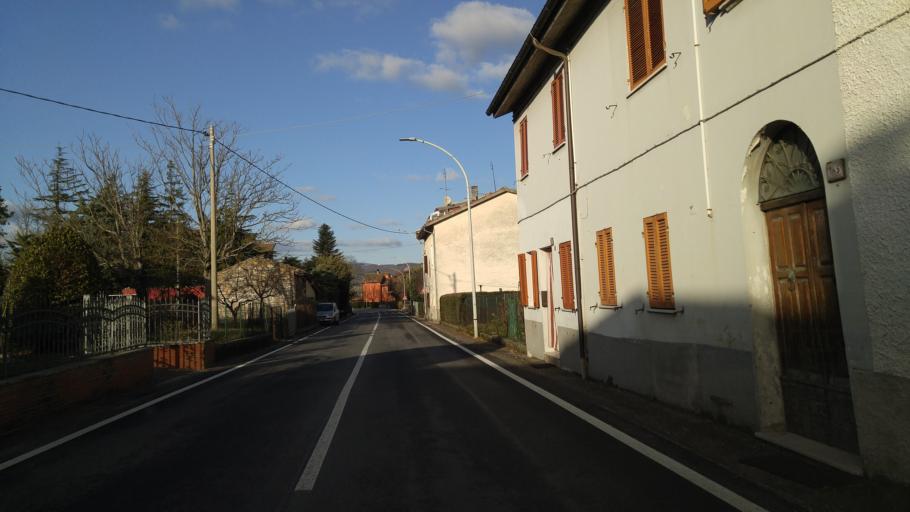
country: IT
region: The Marches
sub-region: Provincia di Pesaro e Urbino
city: Cagli
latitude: 43.5299
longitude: 12.6878
